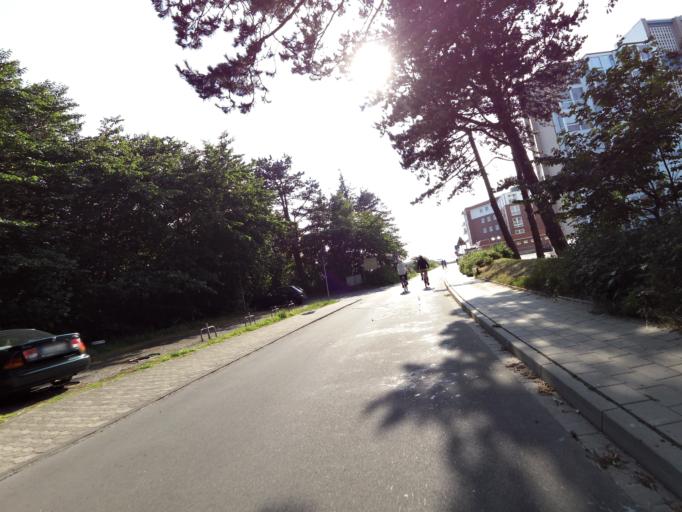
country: DE
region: Lower Saxony
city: Cuxhaven
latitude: 53.8827
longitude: 8.6324
